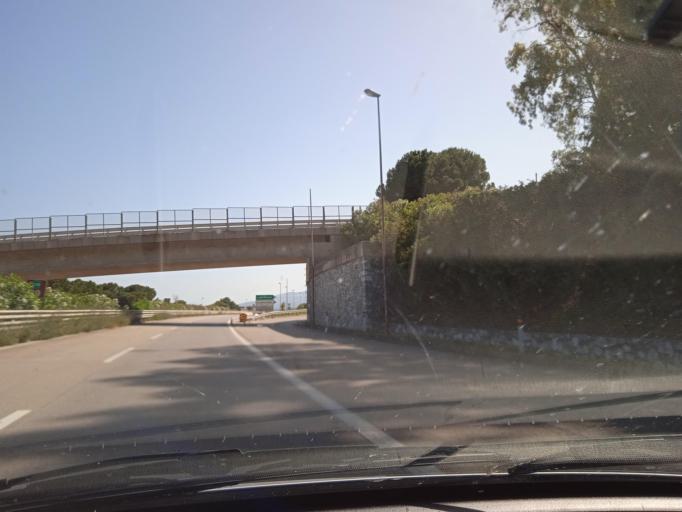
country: IT
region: Sicily
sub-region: Messina
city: Sant'Agata di Militello
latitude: 38.0576
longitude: 14.6207
